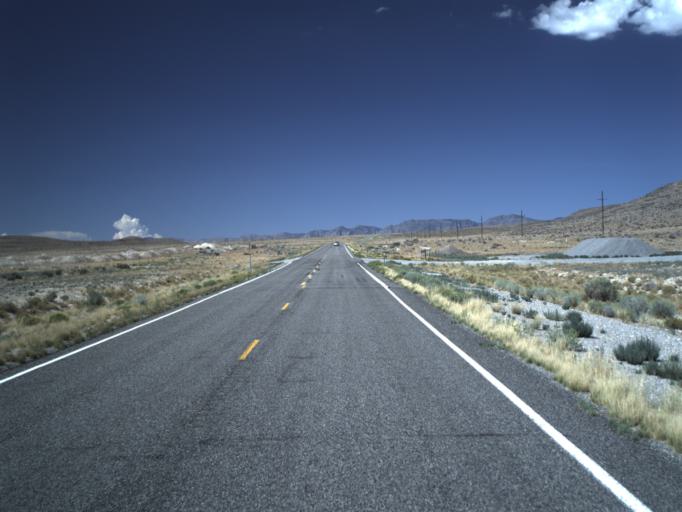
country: US
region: Utah
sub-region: Beaver County
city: Milford
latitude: 39.0596
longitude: -113.2481
